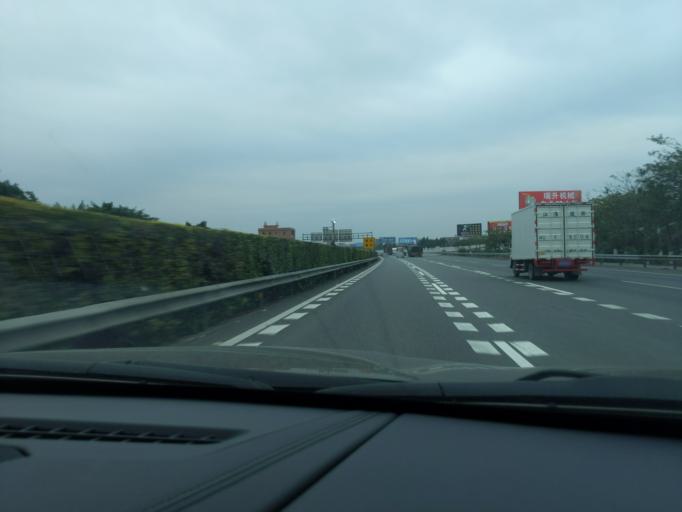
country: CN
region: Fujian
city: Anhai
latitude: 24.7302
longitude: 118.4159
